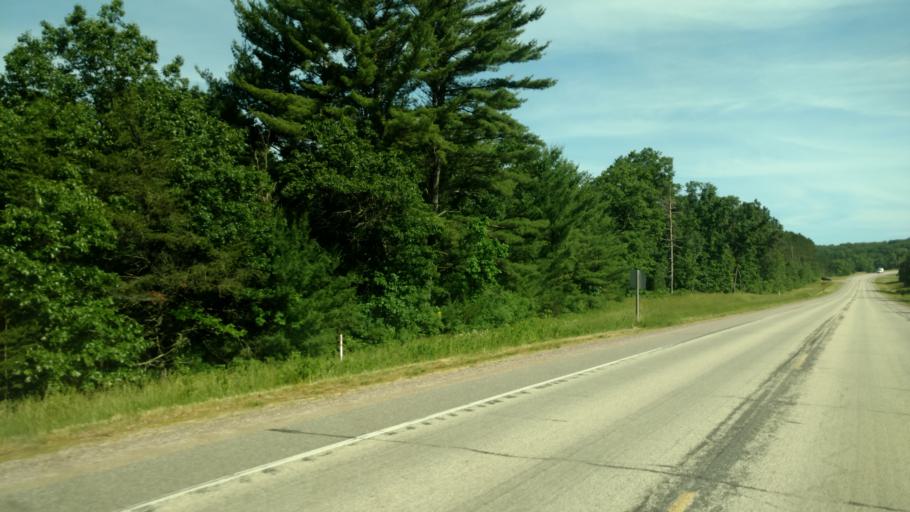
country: US
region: Wisconsin
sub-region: Sauk County
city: Lake Delton
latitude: 43.5757
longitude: -89.8232
